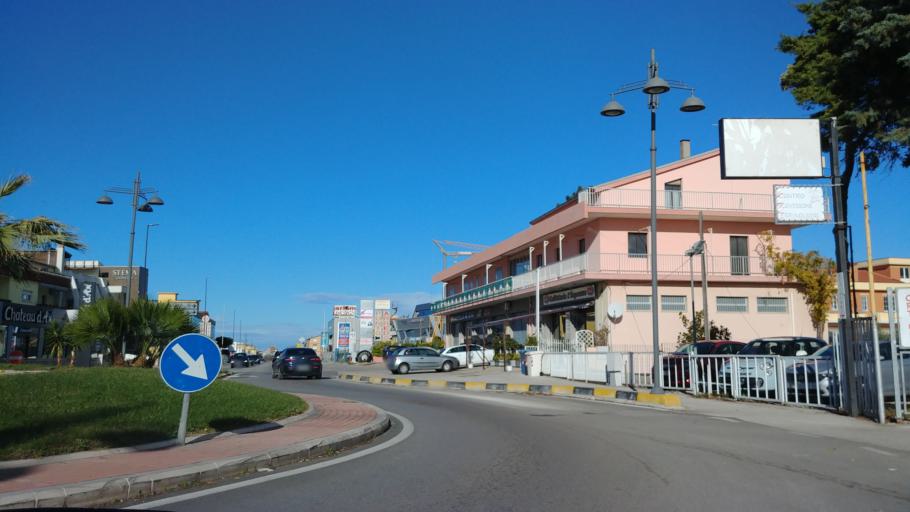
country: IT
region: Molise
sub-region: Provincia di Campobasso
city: Termoli
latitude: 41.9862
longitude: 15.0034
